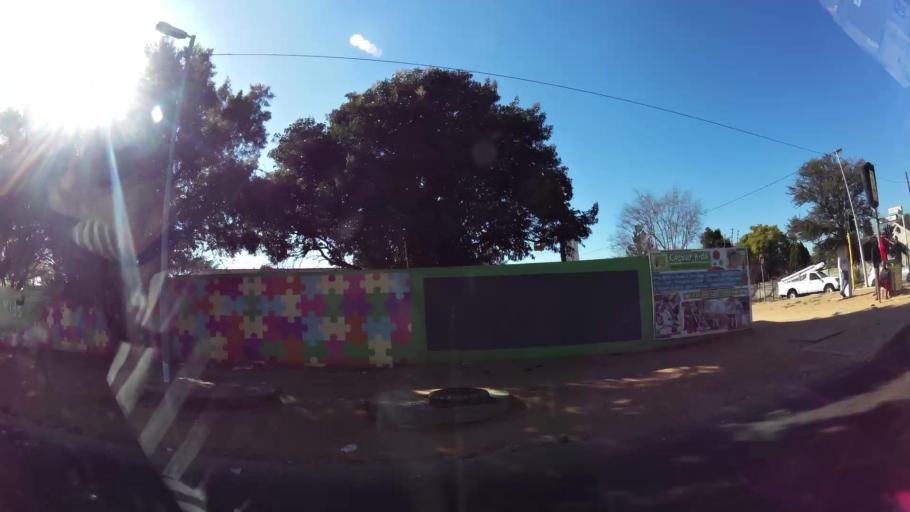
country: ZA
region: Gauteng
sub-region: City of Johannesburg Metropolitan Municipality
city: Diepsloot
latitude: -26.0536
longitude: 27.9740
